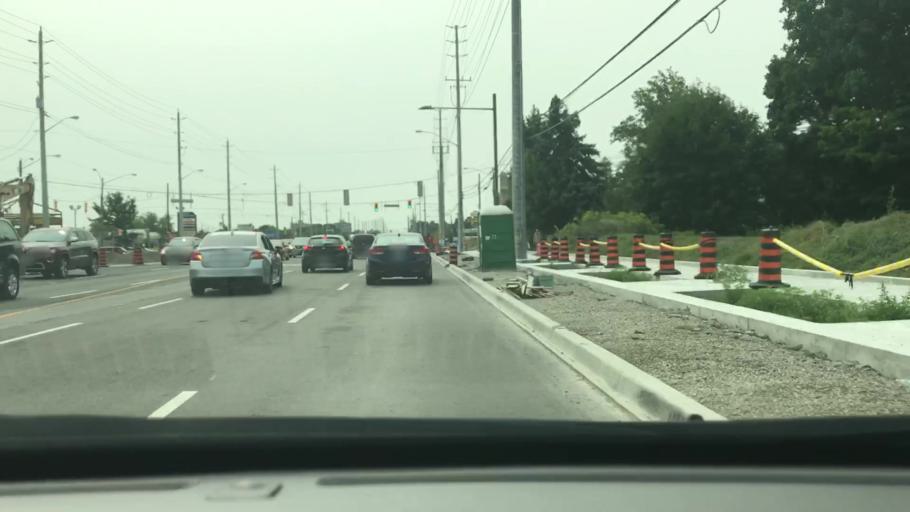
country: CA
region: Ontario
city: Newmarket
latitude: 44.0520
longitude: -79.4799
